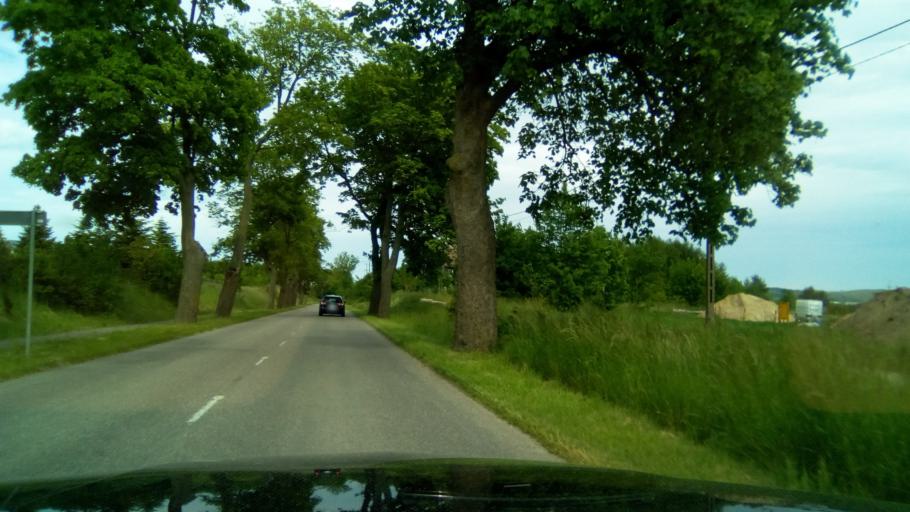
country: PL
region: Pomeranian Voivodeship
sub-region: Powiat pucki
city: Wierzchucino
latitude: 54.7883
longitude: 18.0060
